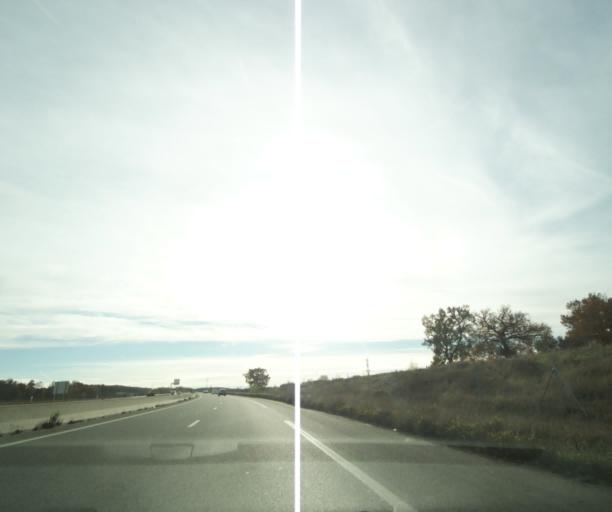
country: FR
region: Midi-Pyrenees
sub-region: Departement de la Haute-Garonne
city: Pibrac
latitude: 43.6005
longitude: 1.2790
